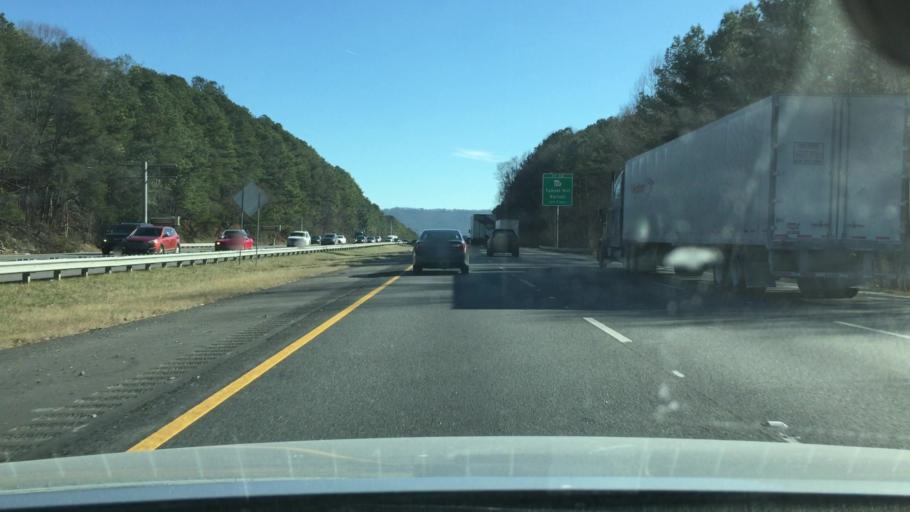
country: US
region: Georgia
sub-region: Whitfield County
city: Varnell
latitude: 34.8742
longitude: -85.0430
